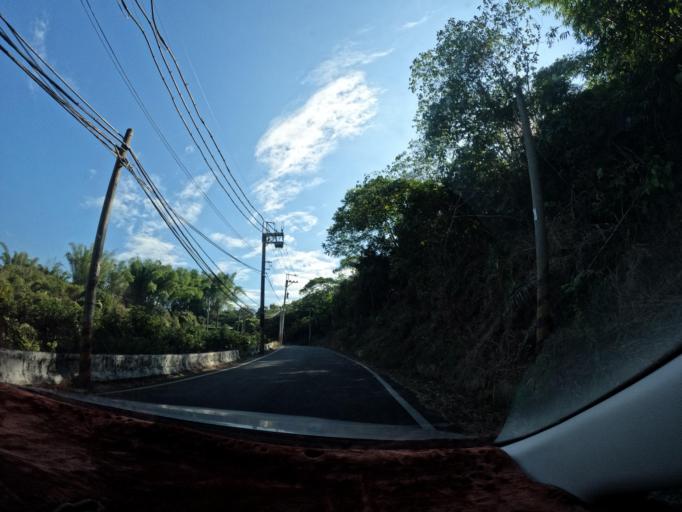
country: TW
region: Taiwan
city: Yujing
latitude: 23.0289
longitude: 120.3931
